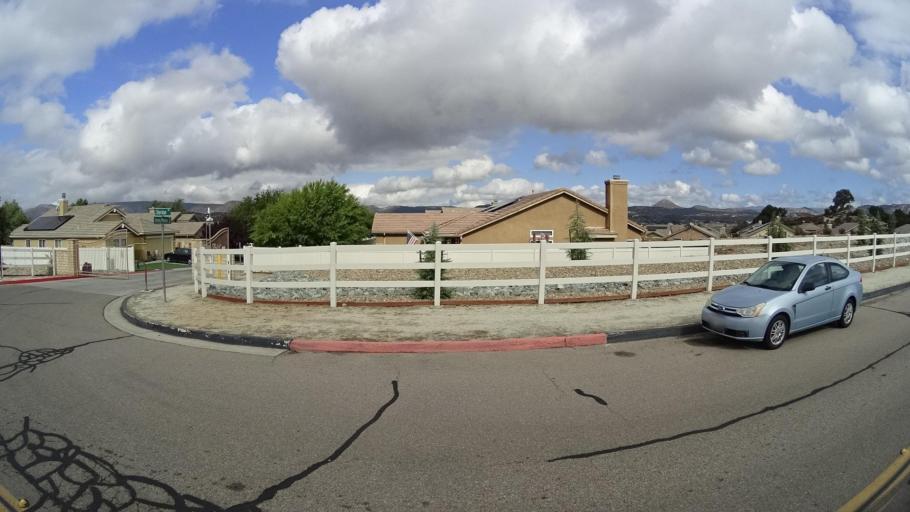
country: US
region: California
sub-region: San Diego County
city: Campo
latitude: 32.6205
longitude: -116.4645
